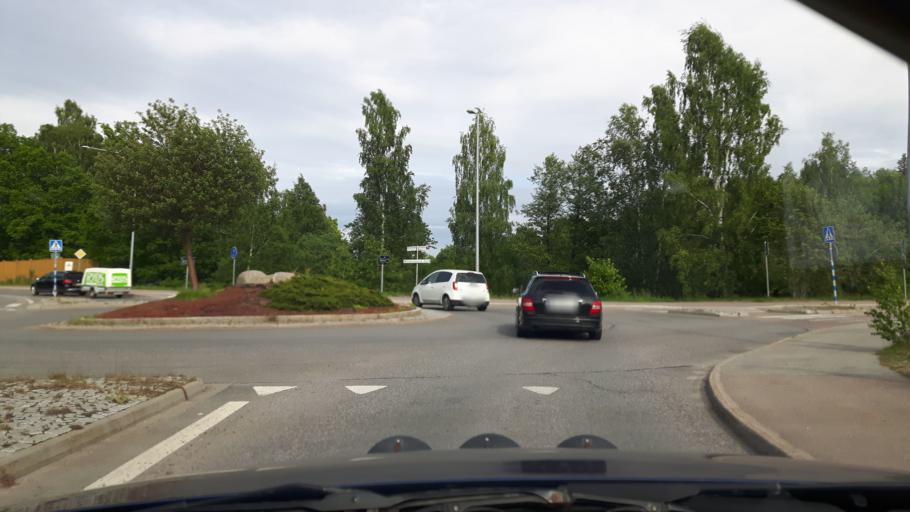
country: SE
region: Stockholm
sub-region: Stockholms Kommun
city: Arsta
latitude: 59.2272
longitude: 18.0848
